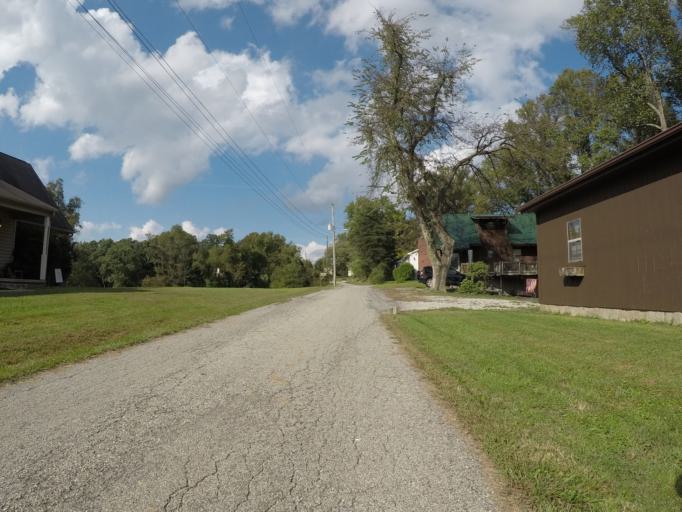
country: US
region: West Virginia
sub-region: Wayne County
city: Lavalette
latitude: 38.3607
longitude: -82.4557
